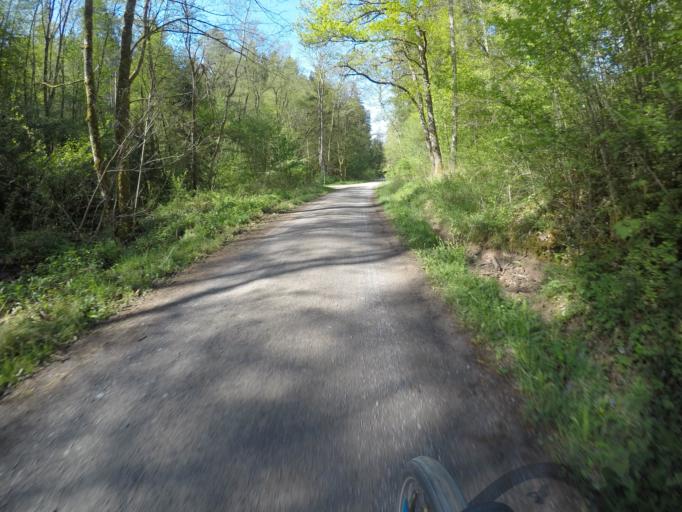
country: DE
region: Baden-Wuerttemberg
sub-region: Tuebingen Region
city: Kusterdingen
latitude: 48.5580
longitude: 9.0880
